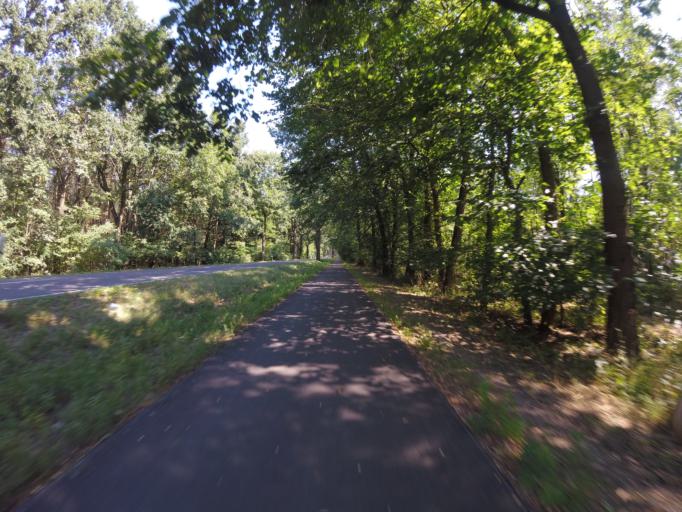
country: DE
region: Brandenburg
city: Mullrose
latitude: 52.2669
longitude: 14.4357
